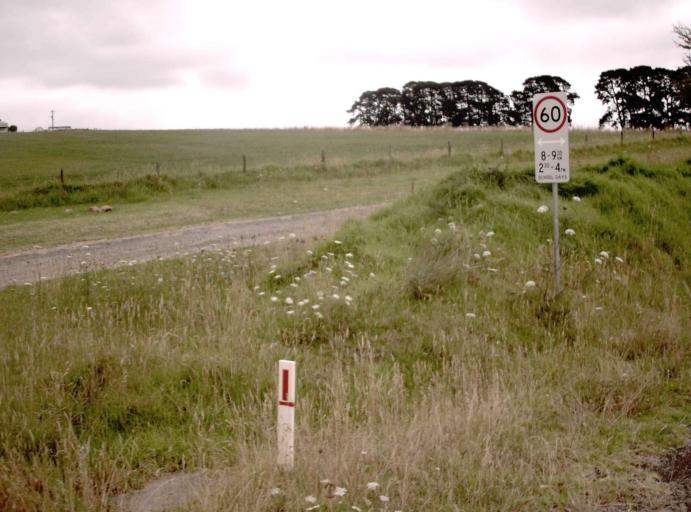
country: AU
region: Victoria
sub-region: Cardinia
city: Bunyip
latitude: -38.2032
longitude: 145.7617
